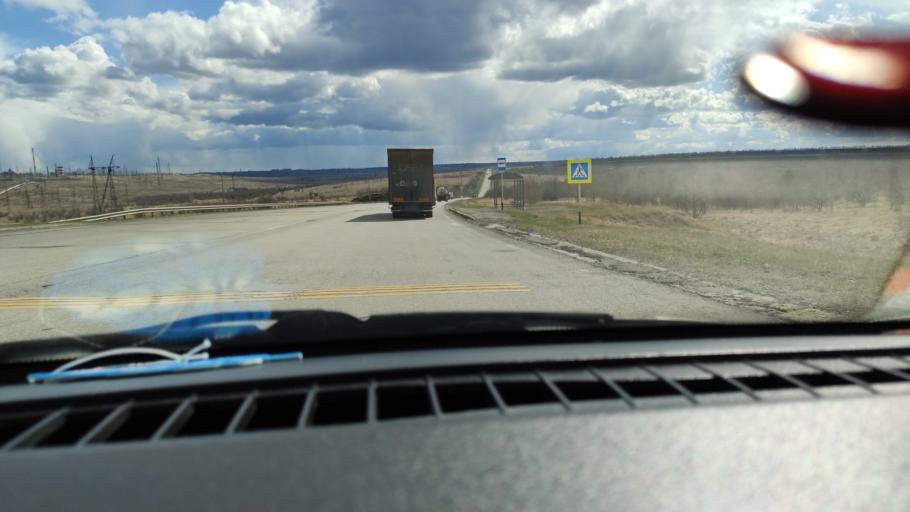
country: RU
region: Samara
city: Varlamovo
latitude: 53.1018
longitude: 48.3567
